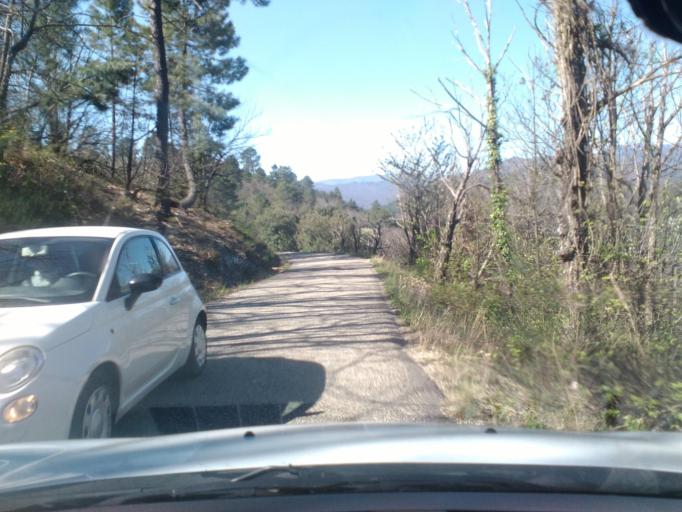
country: FR
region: Languedoc-Roussillon
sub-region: Departement du Gard
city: Saint-Jean-du-Gard
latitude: 44.1409
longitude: 3.7700
